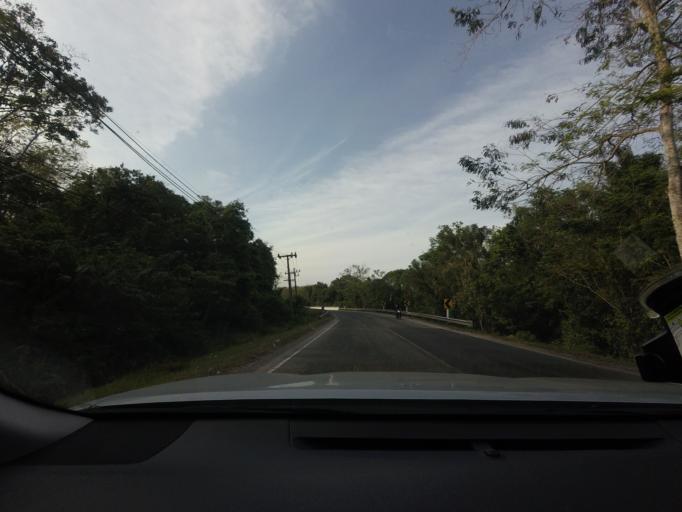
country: TH
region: Narathiwat
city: Ra-ngae
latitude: 6.3311
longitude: 101.7238
